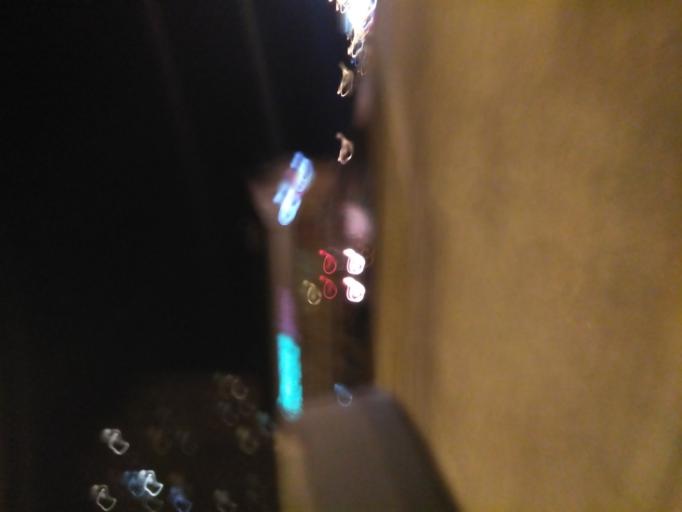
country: RU
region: St.-Petersburg
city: Komendantsky aerodrom
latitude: 60.0193
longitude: 30.2567
